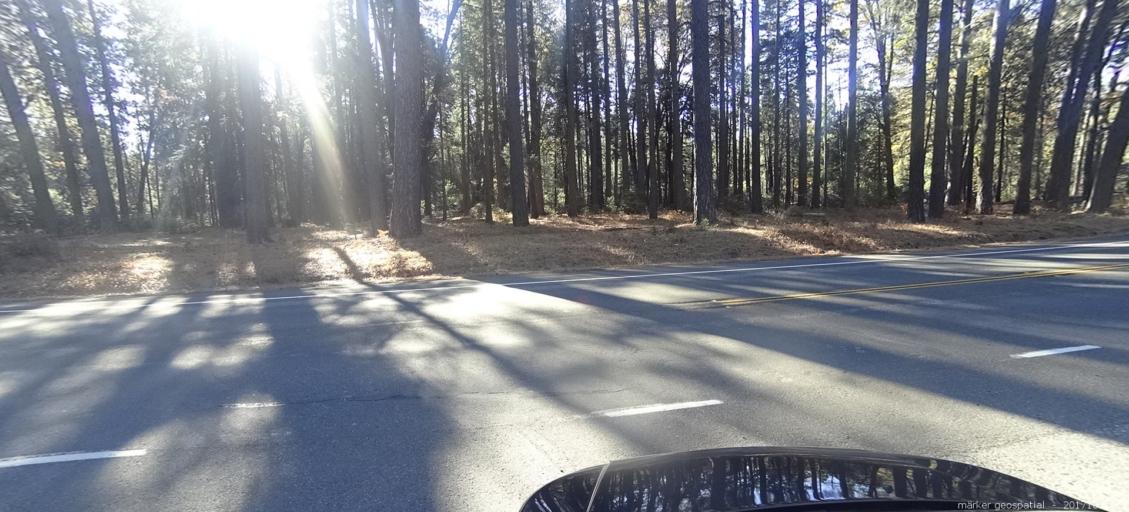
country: US
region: California
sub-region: Shasta County
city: Shingletown
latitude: 40.5079
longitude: -121.8250
